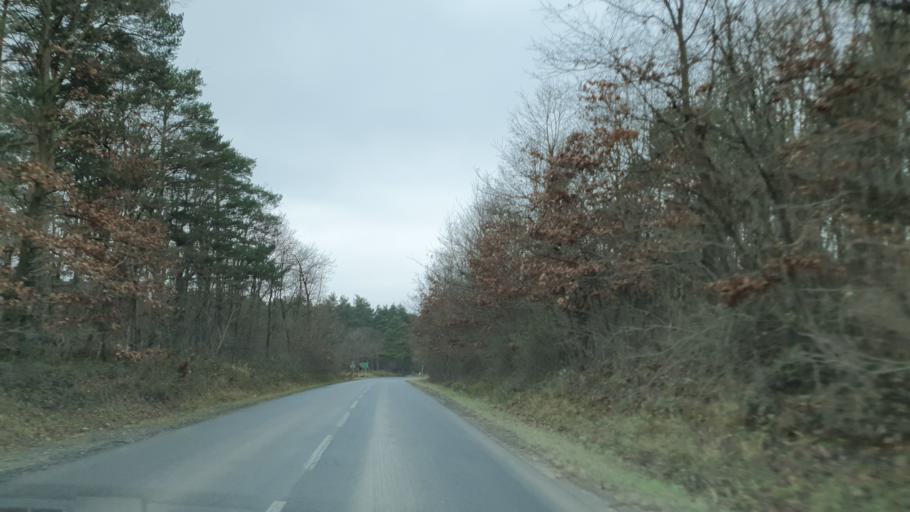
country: HU
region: Veszprem
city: Sumeg
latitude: 46.9648
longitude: 17.3315
